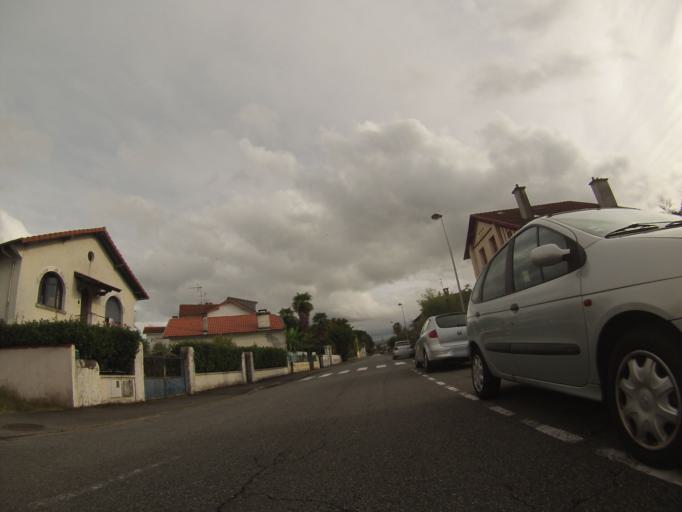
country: FR
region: Aquitaine
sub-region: Departement des Pyrenees-Atlantiques
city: Gelos
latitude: 43.2829
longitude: -0.3768
